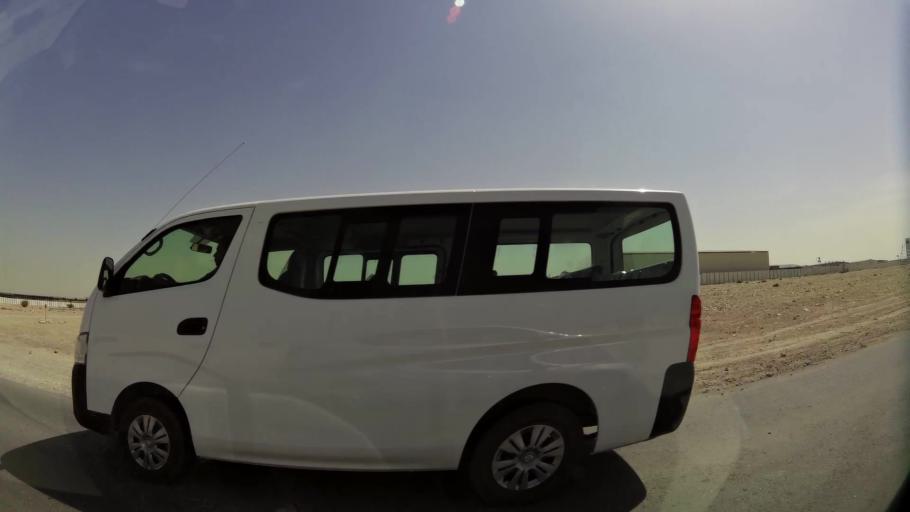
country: QA
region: Baladiyat ar Rayyan
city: Ar Rayyan
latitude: 25.2643
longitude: 51.3831
